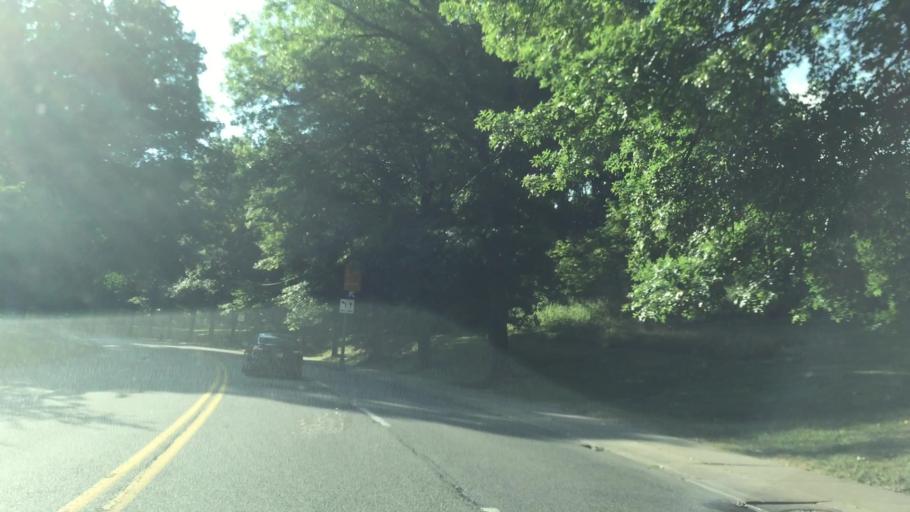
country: US
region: Pennsylvania
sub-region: Allegheny County
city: Bloomfield
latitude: 40.4324
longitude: -79.9358
